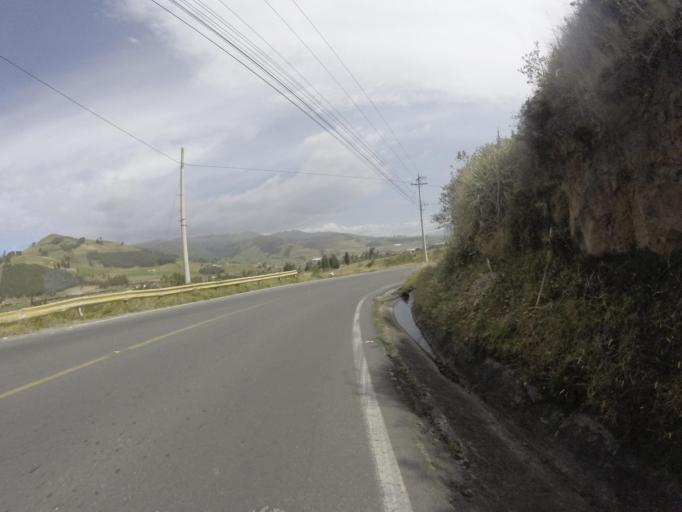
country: EC
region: Pichincha
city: Cayambe
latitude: 0.1235
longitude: -78.0838
